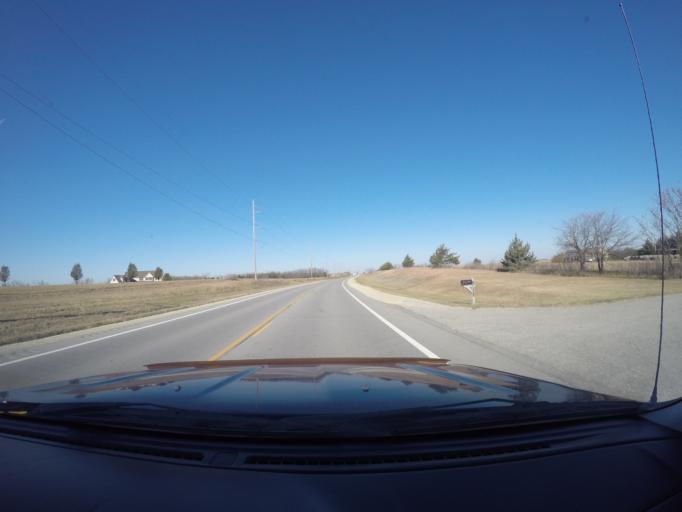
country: US
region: Kansas
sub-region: Riley County
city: Manhattan
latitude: 39.2553
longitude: -96.6740
